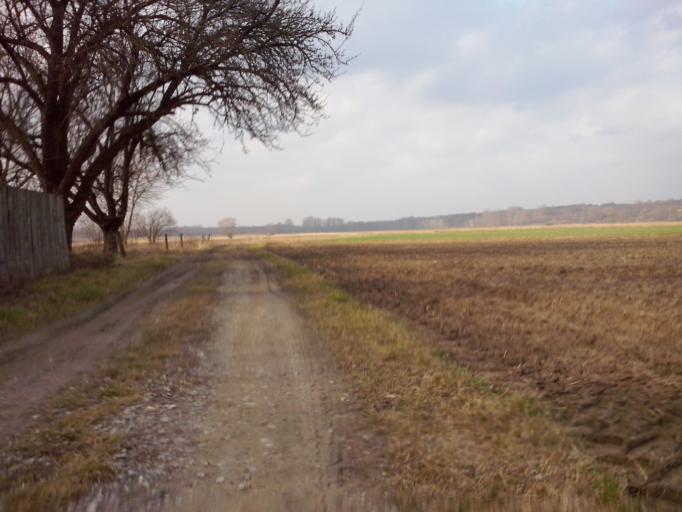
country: PL
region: Subcarpathian Voivodeship
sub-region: Powiat nizanski
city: Krzeszow
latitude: 50.4135
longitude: 22.3234
